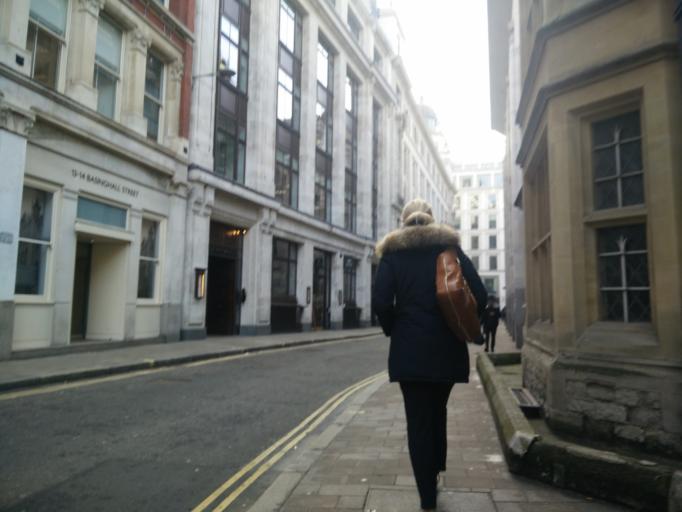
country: GB
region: England
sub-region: Greater London
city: City of London
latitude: 51.5157
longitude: -0.0911
